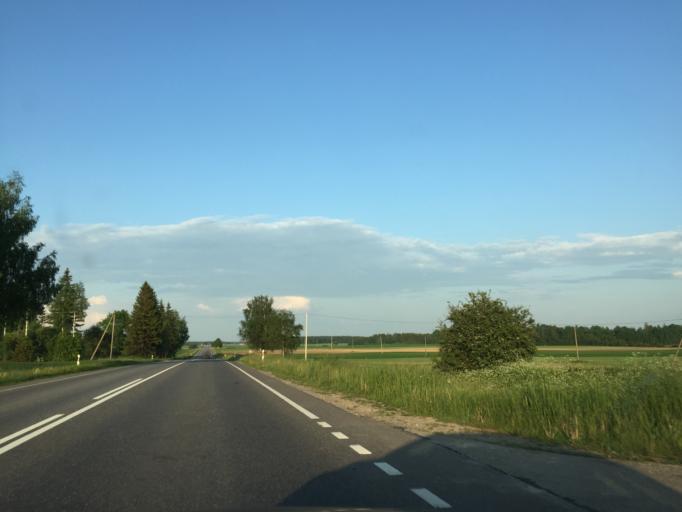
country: LT
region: Telsiu apskritis
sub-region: Telsiai
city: Telsiai
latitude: 56.0033
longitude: 22.3999
